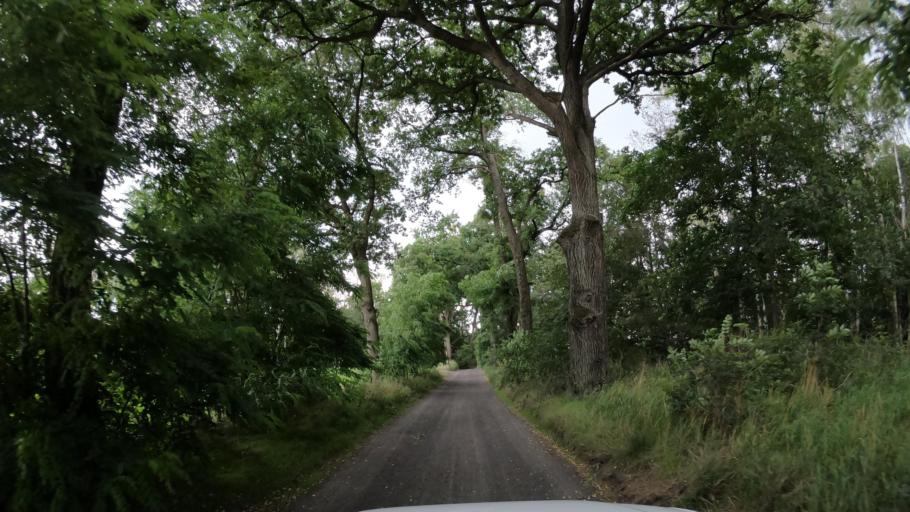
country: PL
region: West Pomeranian Voivodeship
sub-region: Powiat stargardzki
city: Dolice
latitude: 53.1951
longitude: 15.2816
